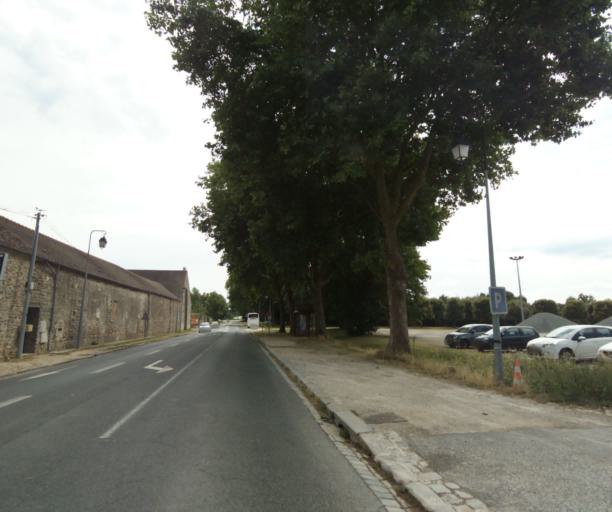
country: FR
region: Ile-de-France
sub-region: Departement de Seine-et-Marne
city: Chailly-en-Biere
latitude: 48.4651
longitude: 2.6072
